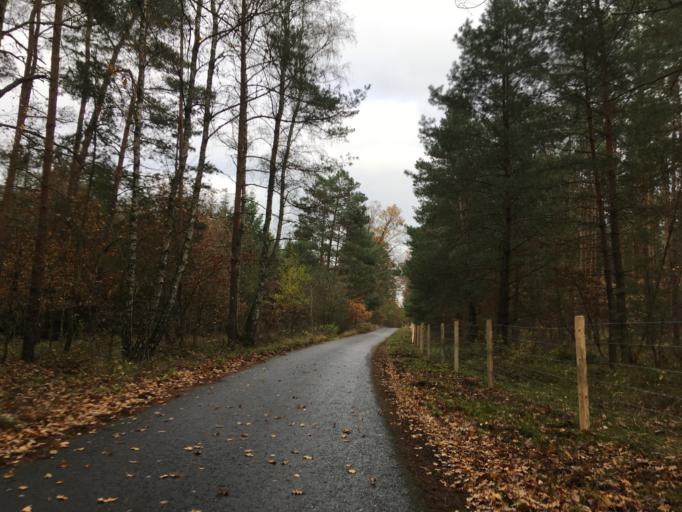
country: DE
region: Brandenburg
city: Jamlitz
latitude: 52.0339
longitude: 14.4687
